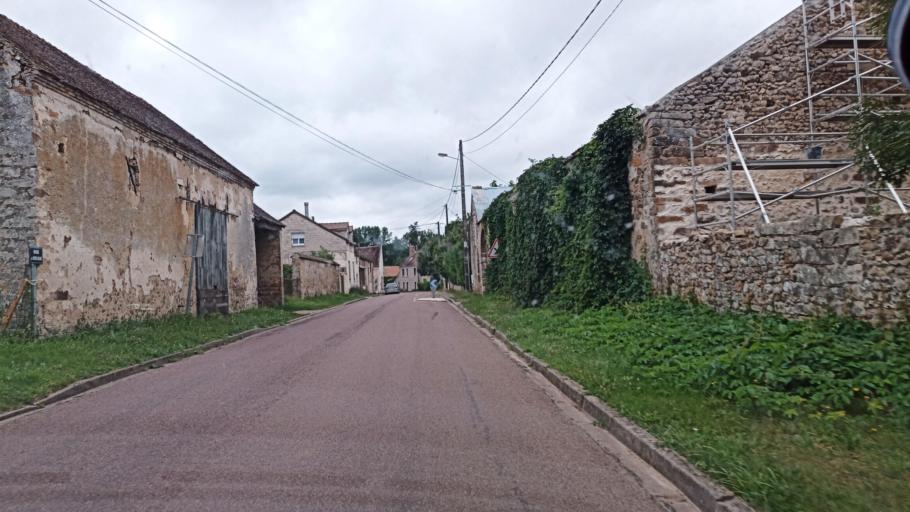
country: FR
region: Ile-de-France
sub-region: Departement de Seine-et-Marne
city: Voulx
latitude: 48.2654
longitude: 3.0088
